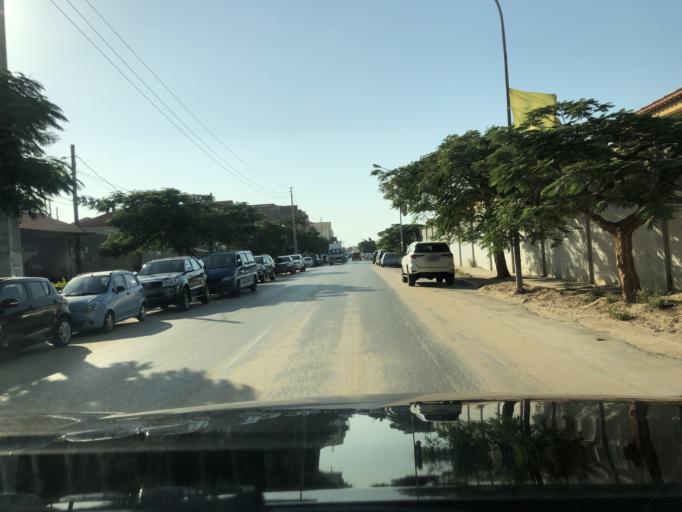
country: AO
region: Luanda
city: Luanda
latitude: -8.9156
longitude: 13.1790
